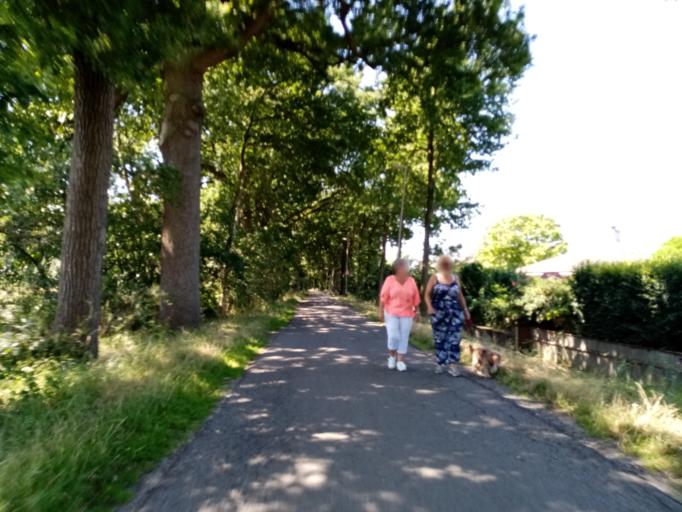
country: NL
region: North Brabant
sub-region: Gemeente Breda
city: Breda
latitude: 51.6159
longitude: 4.7373
